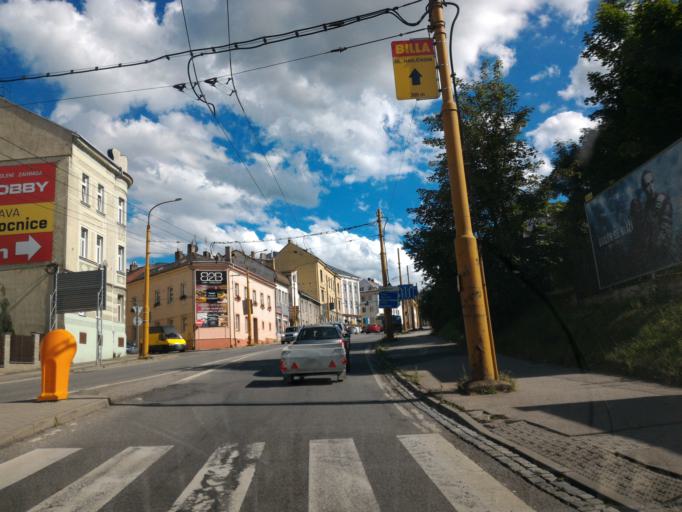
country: CZ
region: Vysocina
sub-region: Okres Jihlava
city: Jihlava
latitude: 49.4042
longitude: 15.5873
